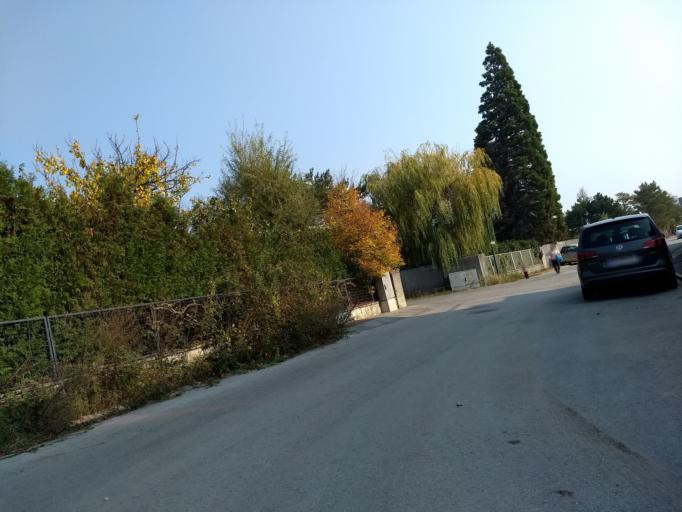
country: AT
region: Lower Austria
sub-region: Politischer Bezirk Modling
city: Perchtoldsdorf
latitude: 48.1294
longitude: 16.2857
